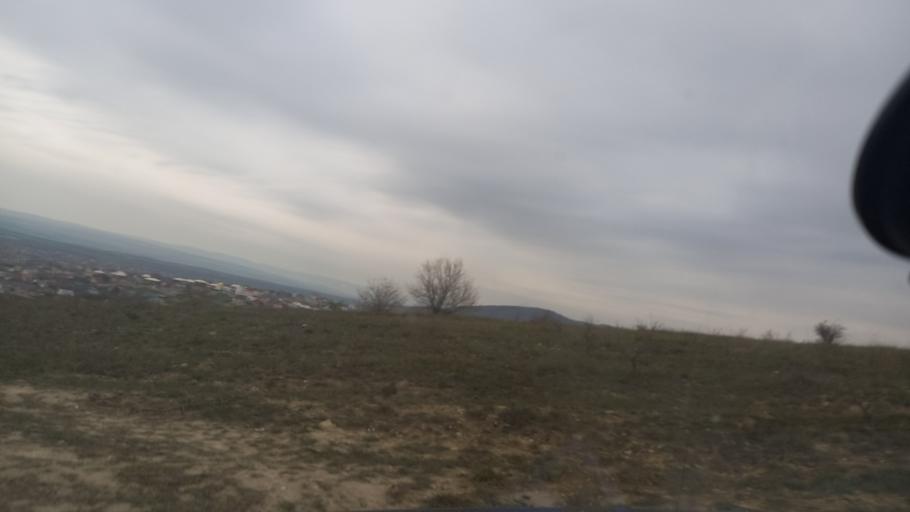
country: RU
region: Krasnodarskiy
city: Anapa
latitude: 44.8513
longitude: 37.3427
